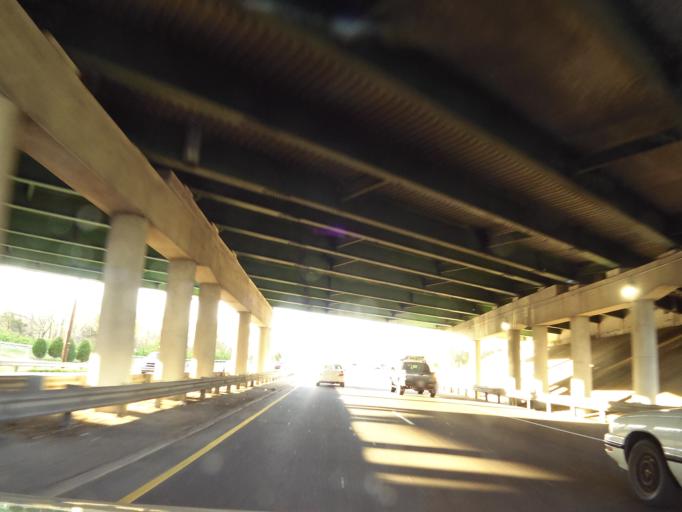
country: US
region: Tennessee
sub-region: Davidson County
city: Goodlettsville
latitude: 36.3083
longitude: -86.7042
